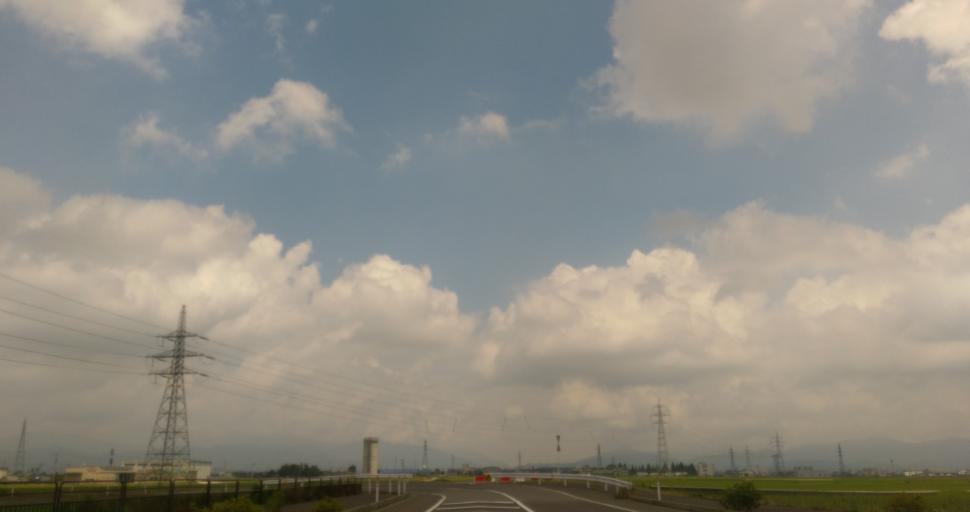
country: JP
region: Fukui
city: Fukui-shi
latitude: 36.1159
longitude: 136.1911
